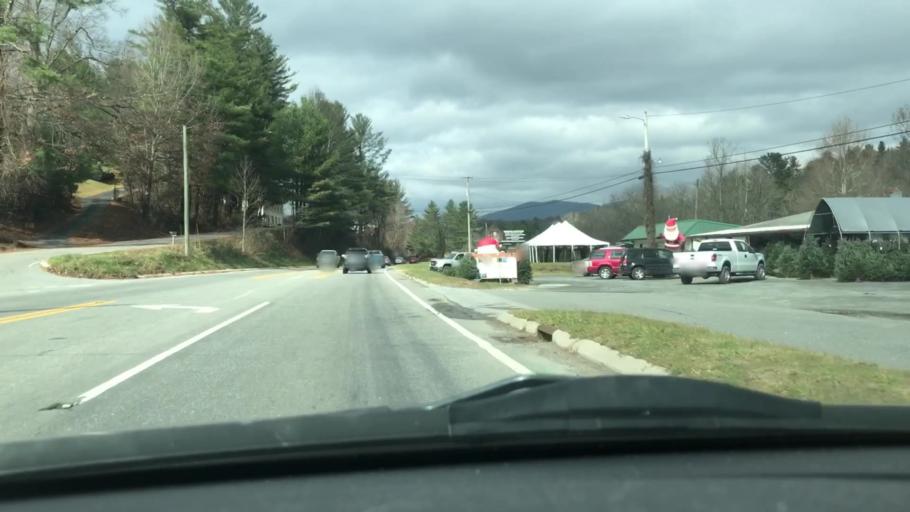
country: US
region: North Carolina
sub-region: Mitchell County
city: Spruce Pine
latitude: 35.8829
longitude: -82.0574
